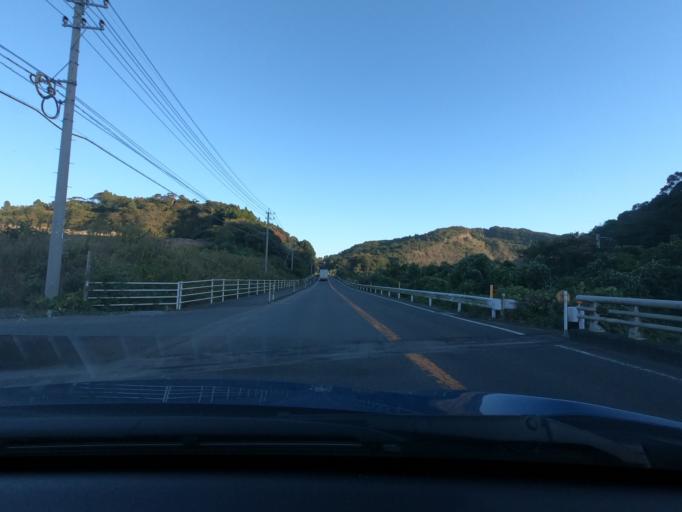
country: JP
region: Kagoshima
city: Satsumasendai
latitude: 31.8463
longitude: 130.2725
